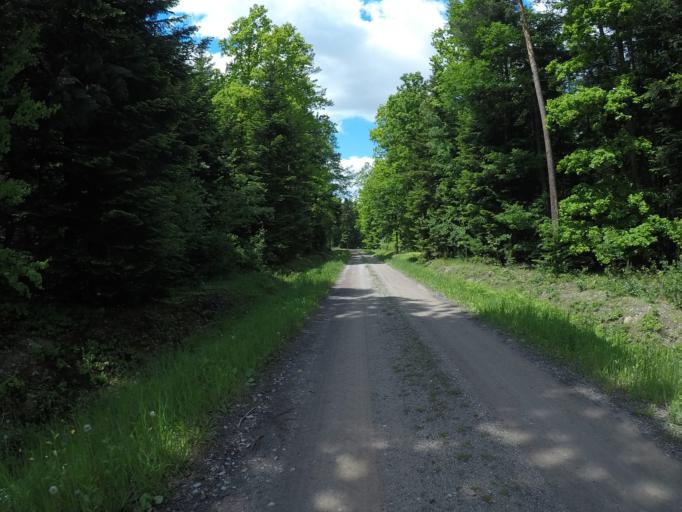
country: PL
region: Swietokrzyskie
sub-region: Powiat kielecki
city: Kostomloty Pierwsze
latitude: 50.9352
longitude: 20.6119
